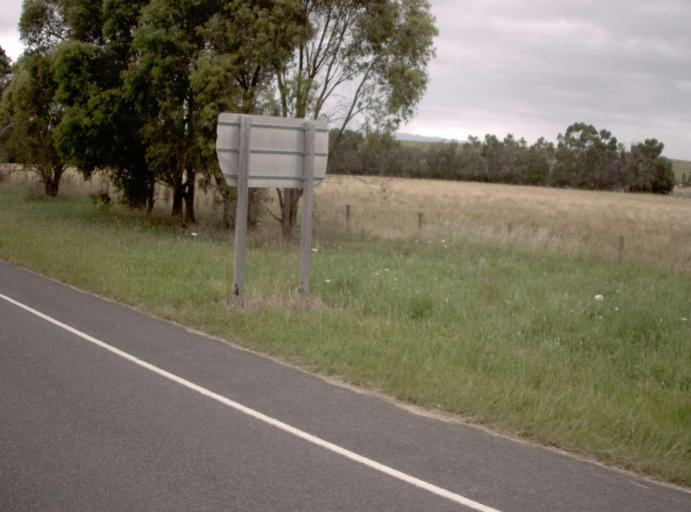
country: AU
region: Victoria
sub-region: Yarra Ranges
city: Yarra Glen
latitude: -37.6476
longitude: 145.3925
